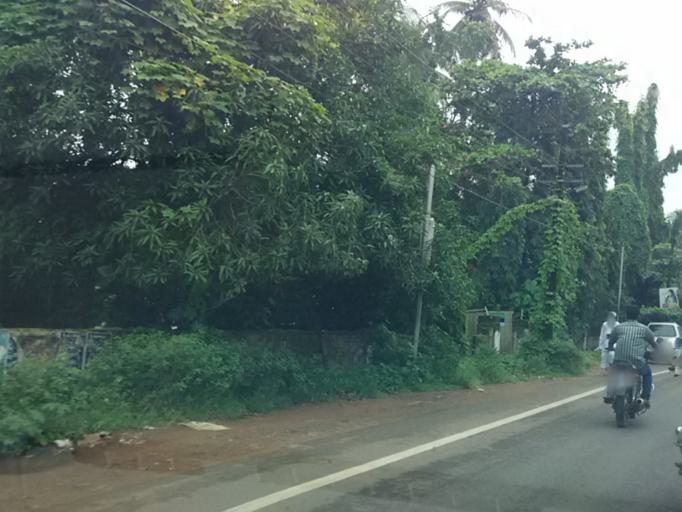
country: IN
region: Kerala
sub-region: Kozhikode
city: Kunnamangalam
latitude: 11.3042
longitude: 75.8725
